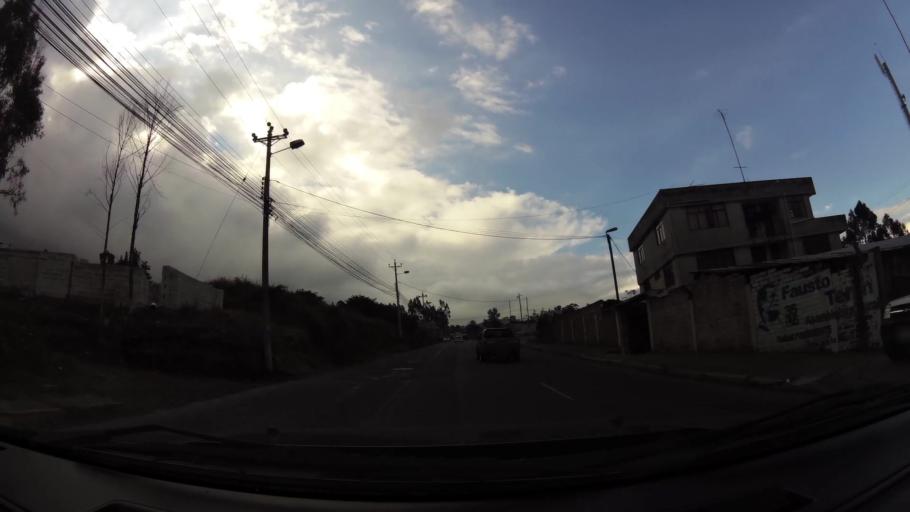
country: EC
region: Pichincha
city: Sangolqui
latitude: -0.2892
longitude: -78.4891
